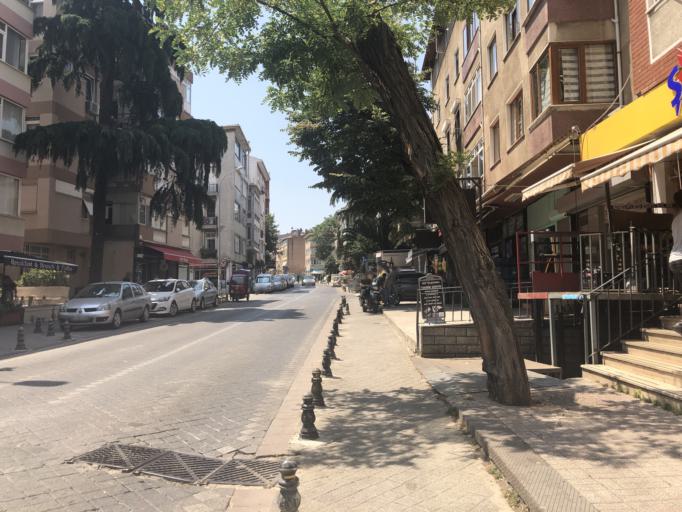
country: TR
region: Istanbul
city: UEskuedar
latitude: 40.9875
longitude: 29.0315
